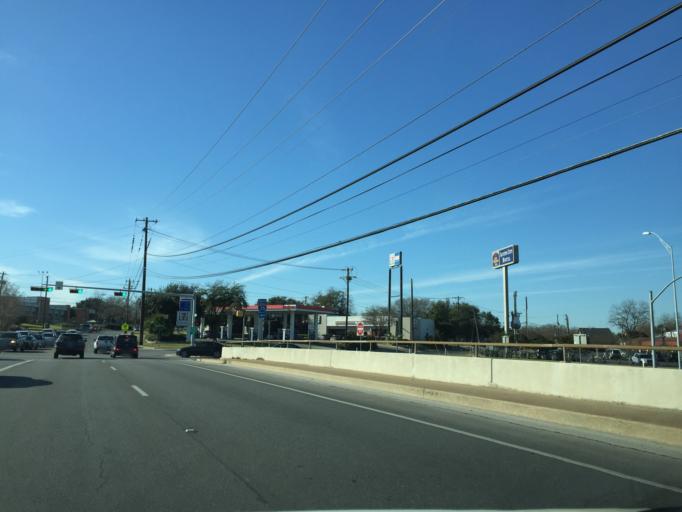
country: US
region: Texas
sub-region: Travis County
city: Austin
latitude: 30.2338
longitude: -97.7410
